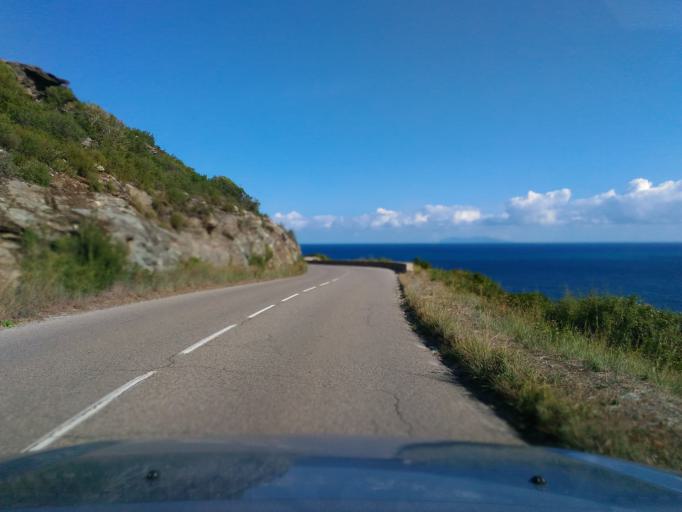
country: FR
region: Corsica
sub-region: Departement de la Haute-Corse
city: Brando
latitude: 42.8008
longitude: 9.4899
